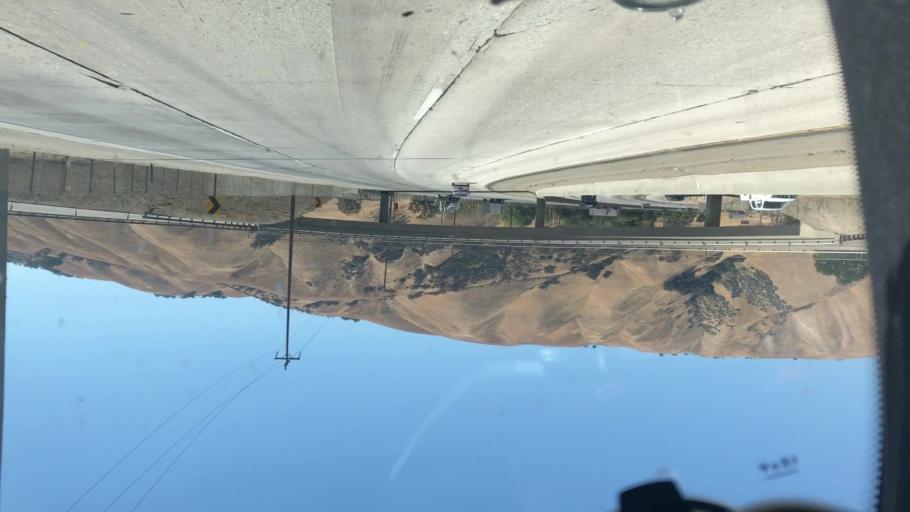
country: US
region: California
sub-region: Kern County
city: Lebec
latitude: 34.8347
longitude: -118.8643
